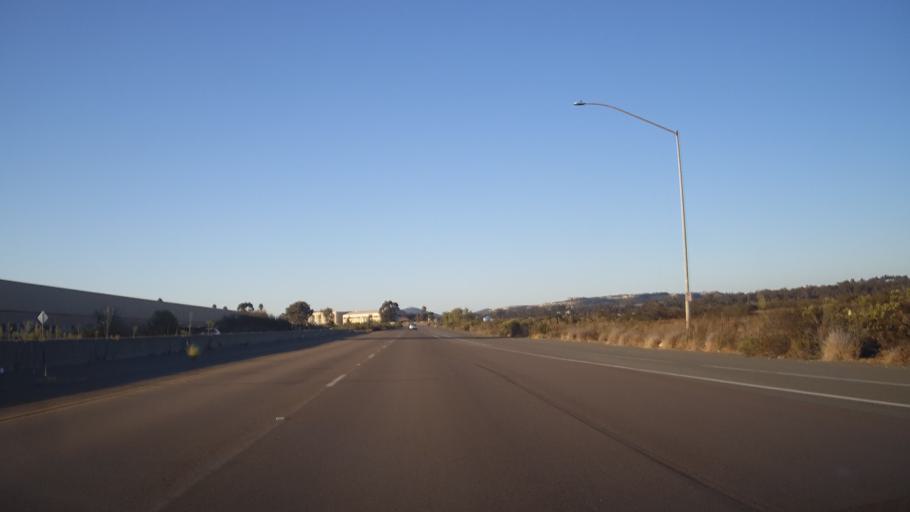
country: US
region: California
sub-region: San Diego County
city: Poway
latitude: 32.8840
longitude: -117.1165
